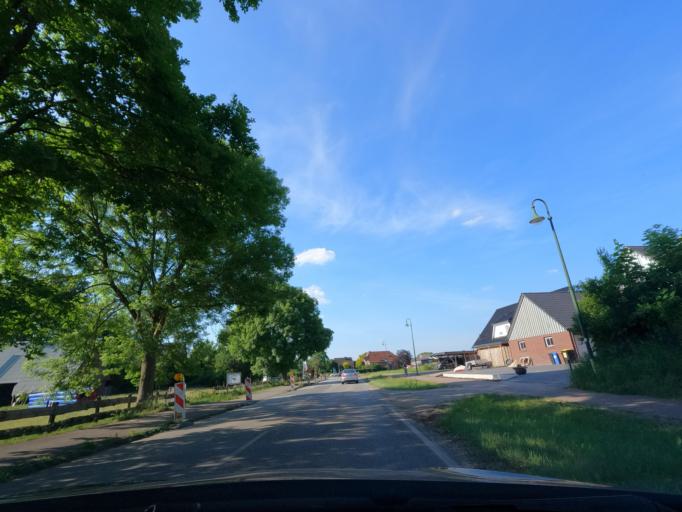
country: DE
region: Schleswig-Holstein
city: Gross Nordende
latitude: 53.7007
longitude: 9.6496
